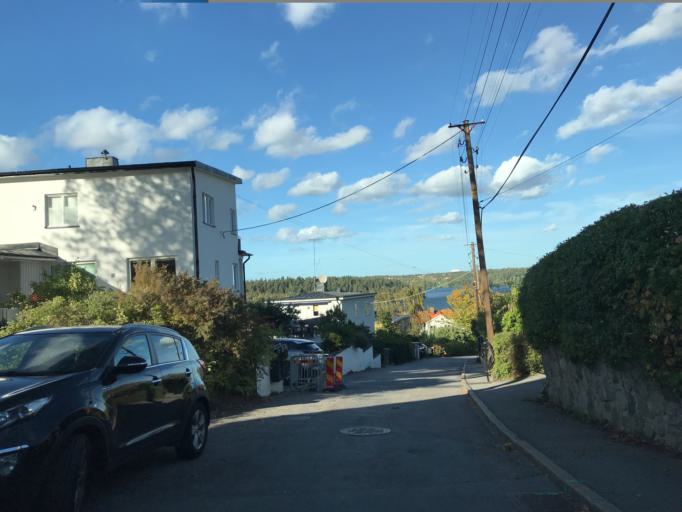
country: SE
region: Stockholm
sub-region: Huddinge Kommun
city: Segeltorp
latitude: 59.3015
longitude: 17.9424
